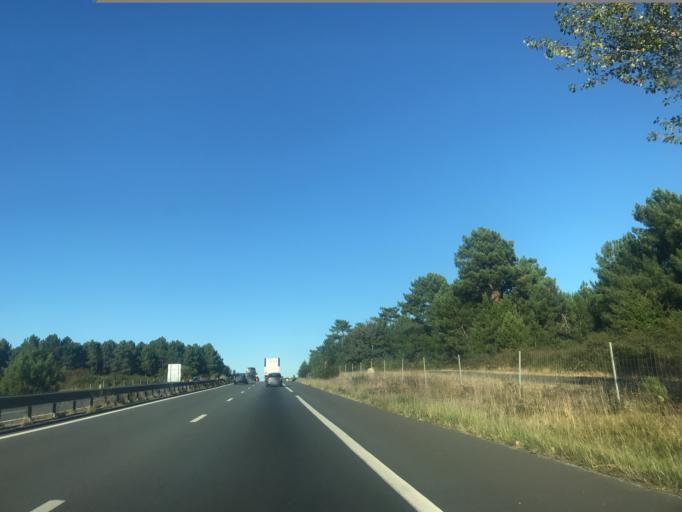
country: FR
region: Aquitaine
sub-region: Departement de la Gironde
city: Laruscade
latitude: 45.1803
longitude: -0.3246
